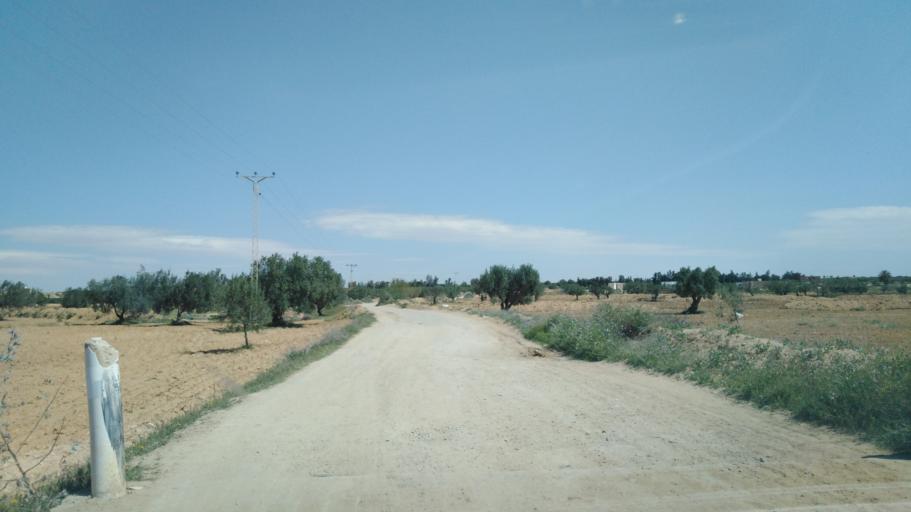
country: TN
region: Safaqis
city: Sfax
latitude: 34.7524
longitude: 10.5279
